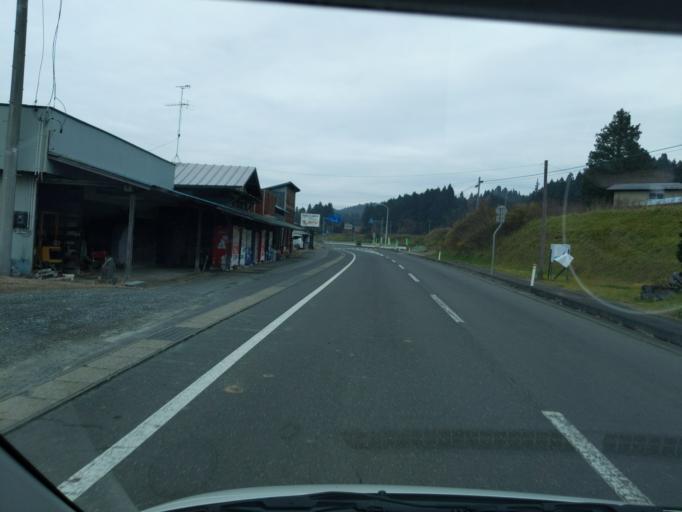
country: JP
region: Iwate
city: Mizusawa
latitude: 39.1725
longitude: 141.2139
